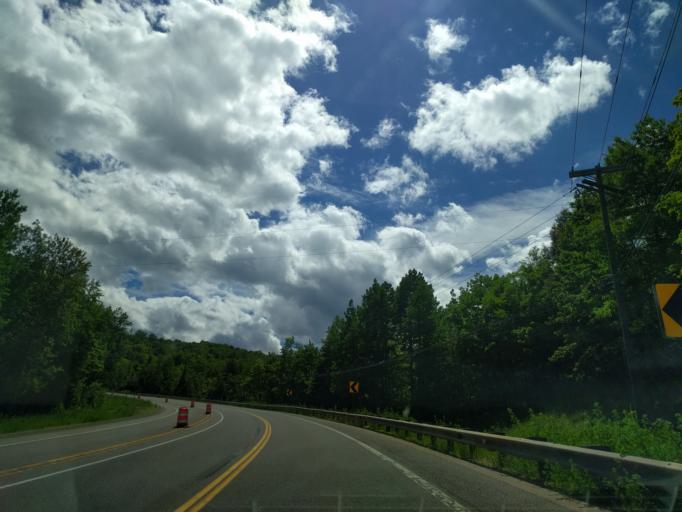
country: US
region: Michigan
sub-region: Marquette County
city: Marquette
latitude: 46.5069
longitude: -87.4265
